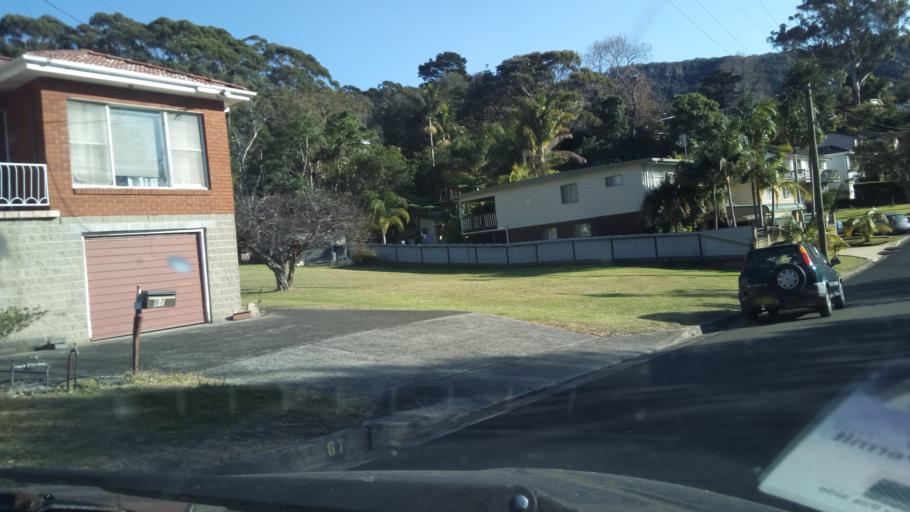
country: AU
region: New South Wales
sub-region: Wollongong
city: Bulli
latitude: -34.3194
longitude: 150.9101
